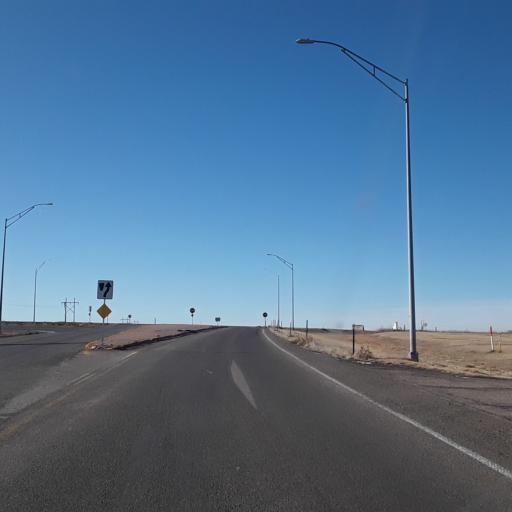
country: US
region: Nebraska
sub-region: Frontier County
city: Stockville
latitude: 40.6566
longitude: -100.6395
